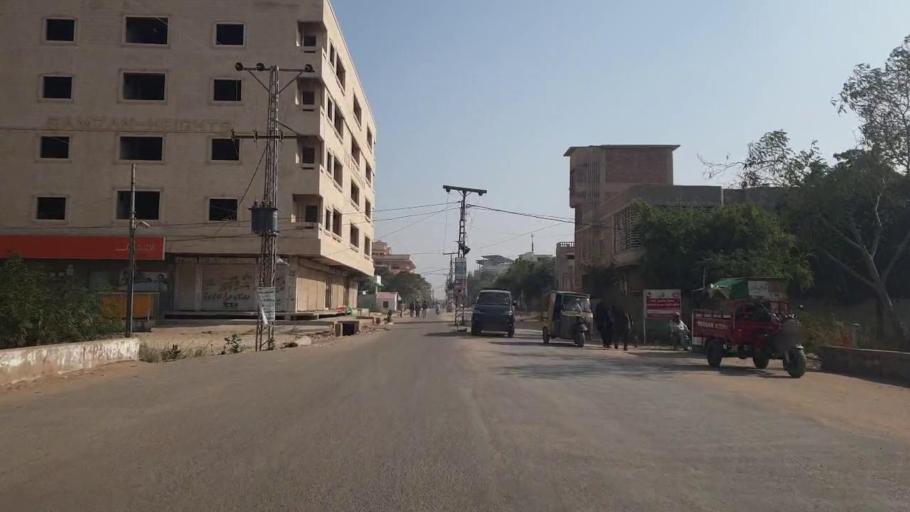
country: PK
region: Sindh
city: Jamshoro
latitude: 25.4138
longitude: 68.2729
